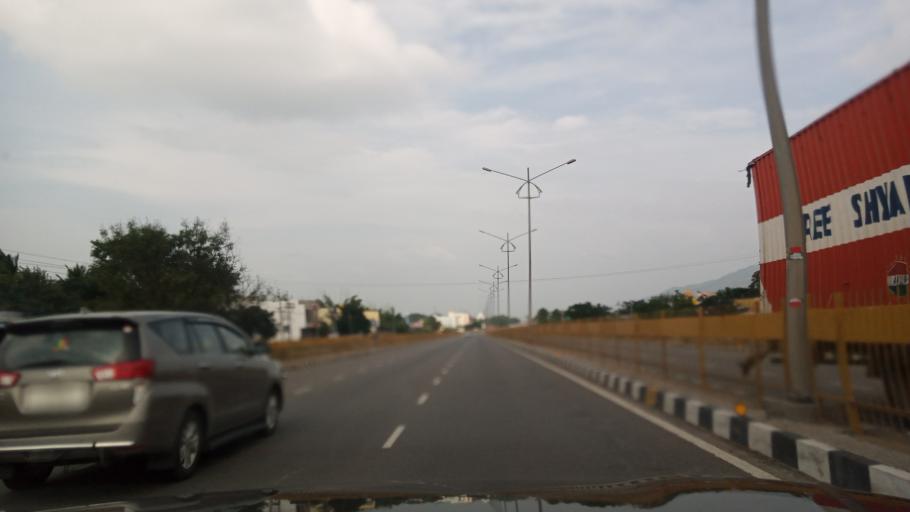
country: IN
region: Tamil Nadu
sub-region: Vellore
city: Vaniyambadi
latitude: 12.6696
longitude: 78.6156
